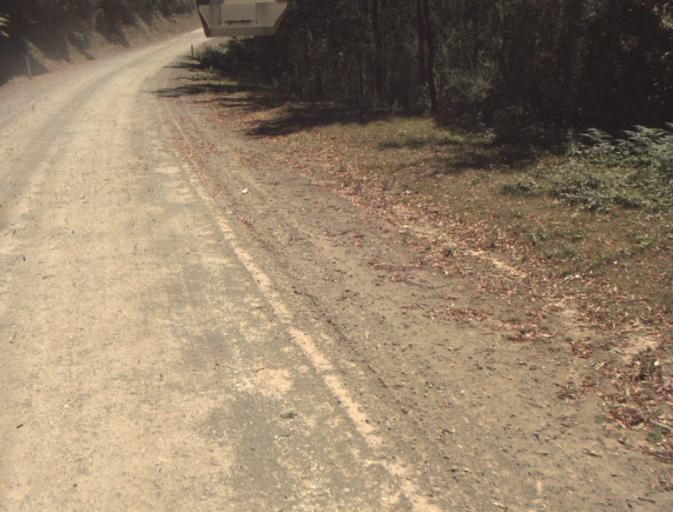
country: AU
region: Tasmania
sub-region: Dorset
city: Scottsdale
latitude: -41.3183
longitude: 147.4092
